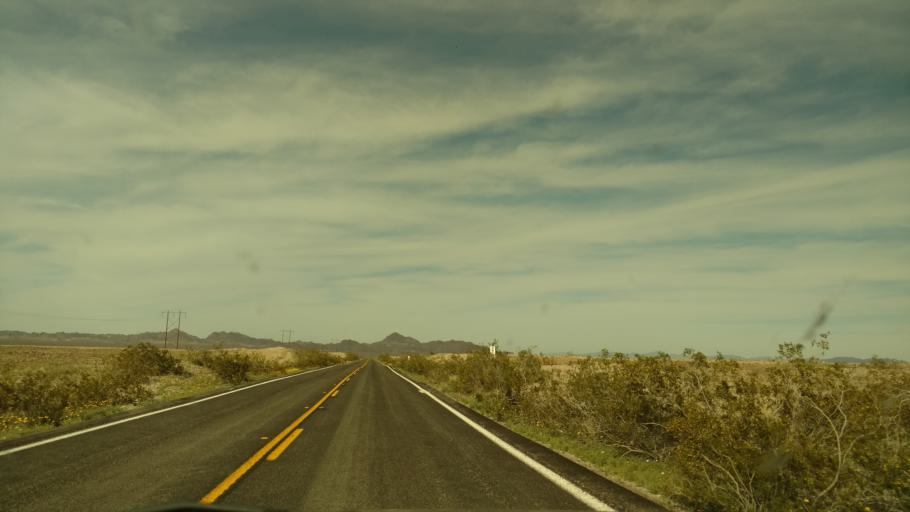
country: US
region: California
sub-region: Riverside County
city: Mesa Verde
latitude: 33.2265
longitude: -114.8487
